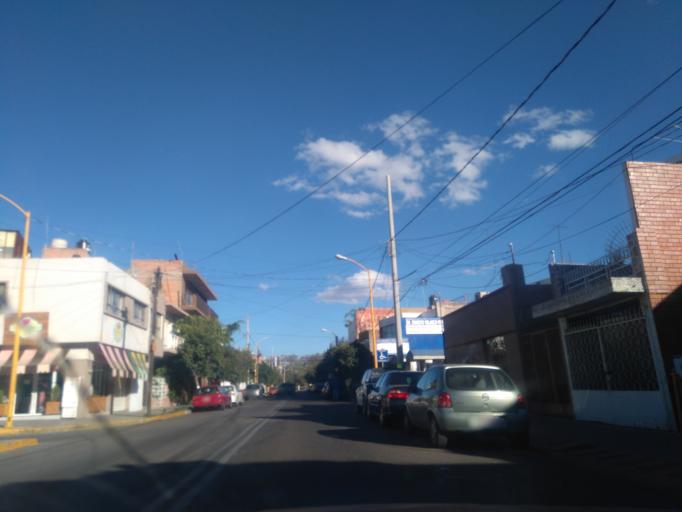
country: MX
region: Aguascalientes
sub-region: Aguascalientes
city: Aguascalientes
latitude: 21.8800
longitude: -102.3071
